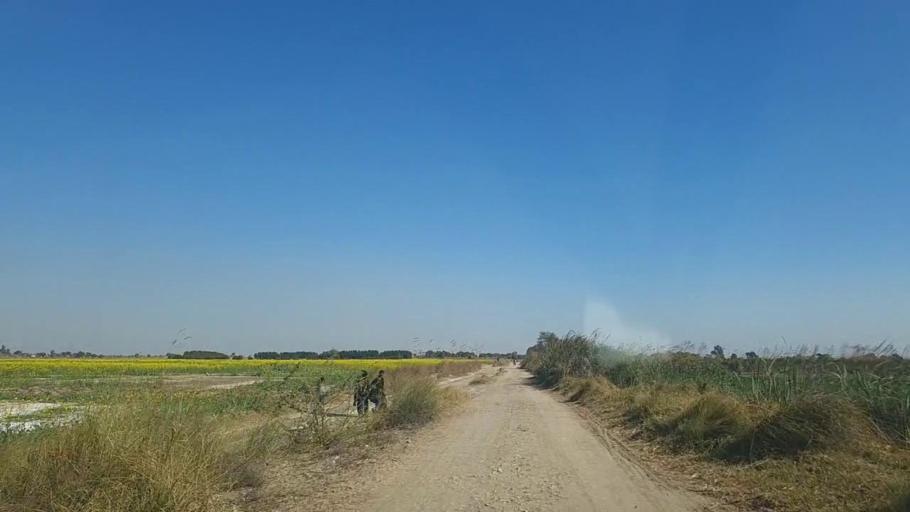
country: PK
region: Sindh
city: Sanghar
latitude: 26.2092
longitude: 68.9009
